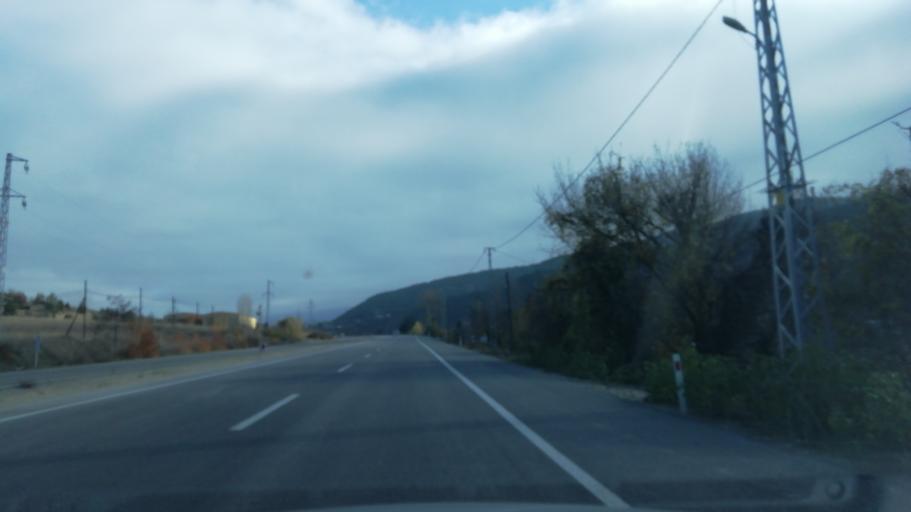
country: TR
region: Karabuk
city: Safranbolu
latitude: 41.2175
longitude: 32.7492
